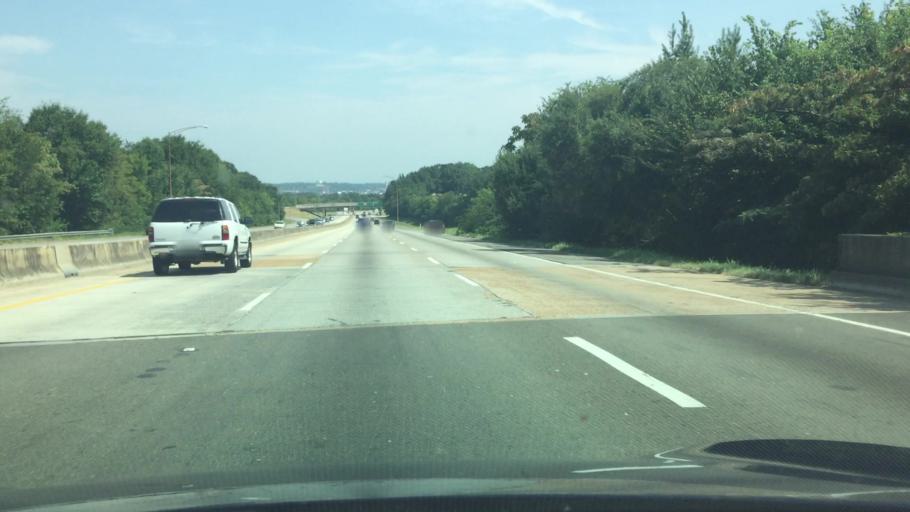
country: US
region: Alabama
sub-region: Jefferson County
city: Homewood
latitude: 33.4777
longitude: -86.8277
